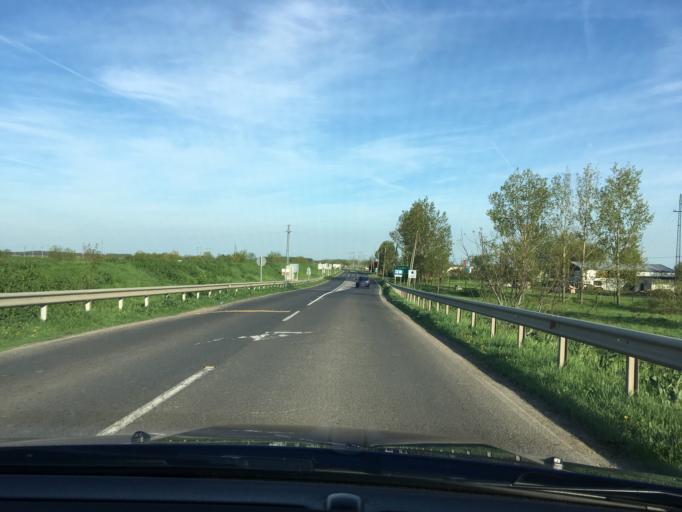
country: HU
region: Bekes
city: Szeghalom
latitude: 47.0128
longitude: 21.1802
